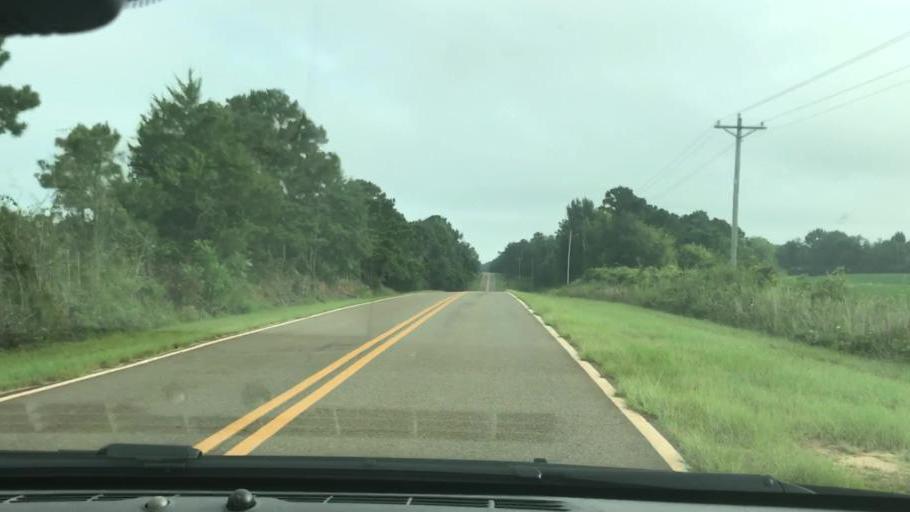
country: US
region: Georgia
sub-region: Stewart County
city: Lumpkin
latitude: 32.0263
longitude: -84.9128
